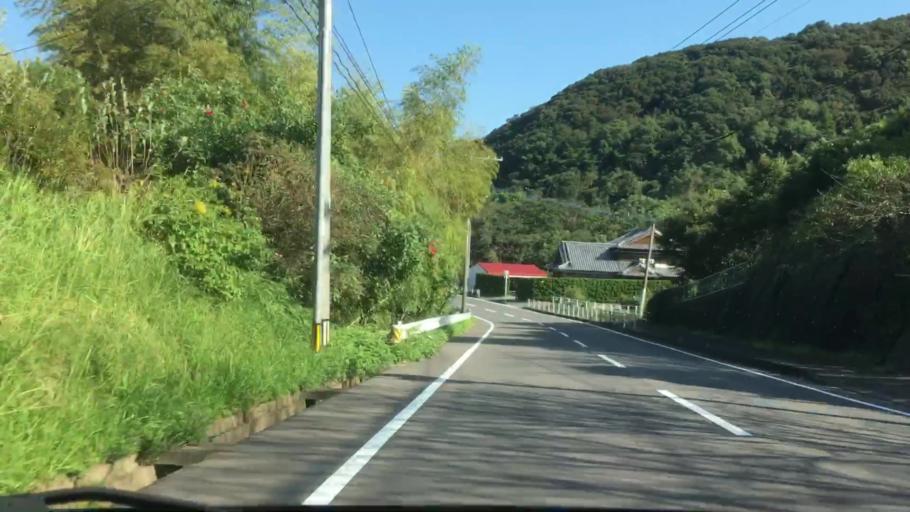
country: JP
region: Nagasaki
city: Sasebo
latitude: 33.0073
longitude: 129.6570
